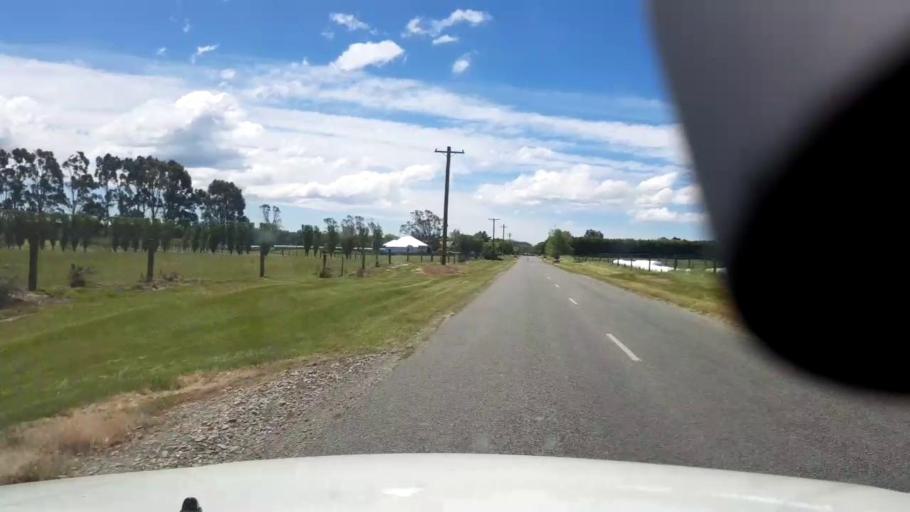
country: NZ
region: Canterbury
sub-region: Timaru District
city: Pleasant Point
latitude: -44.2747
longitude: 171.2529
